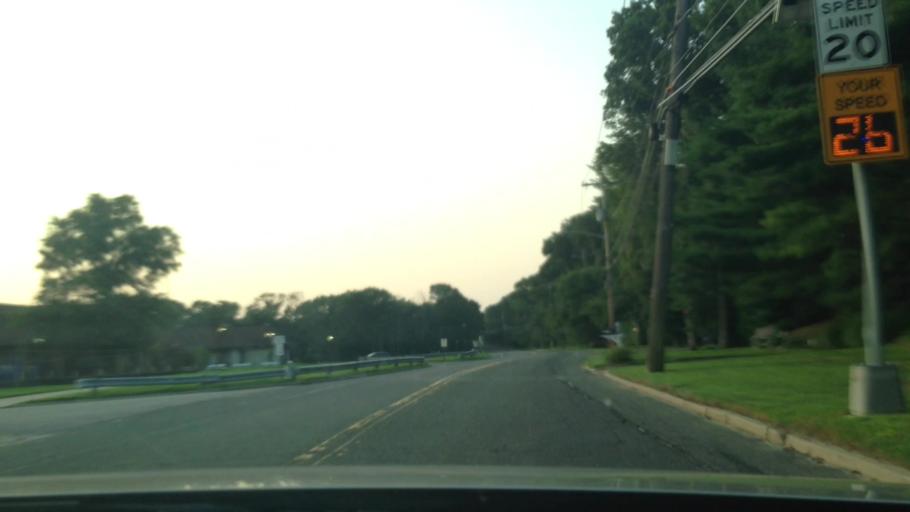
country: US
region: New York
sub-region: Suffolk County
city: South Huntington
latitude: 40.8038
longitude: -73.3796
